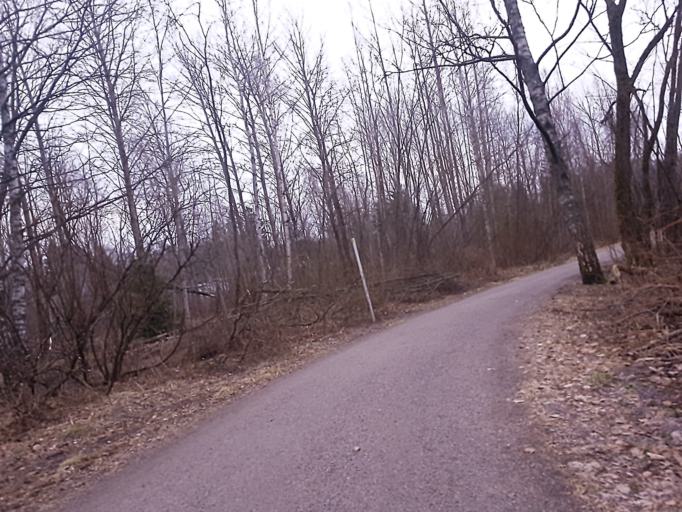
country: FI
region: Uusimaa
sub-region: Helsinki
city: Helsinki
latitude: 60.2294
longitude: 24.9186
